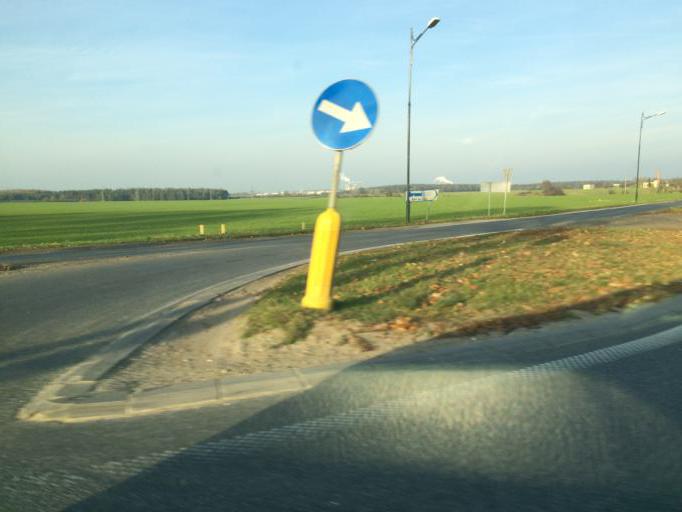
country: PL
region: Opole Voivodeship
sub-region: Powiat strzelecki
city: Strzelce Opolskie
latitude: 50.5256
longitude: 18.2734
